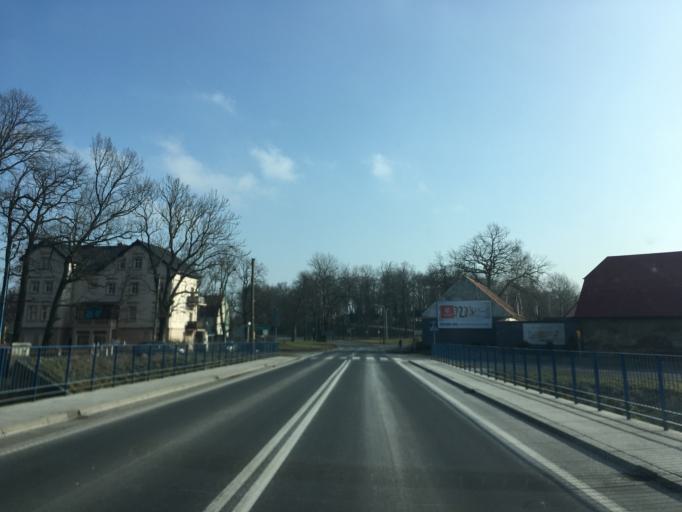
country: PL
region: Lower Silesian Voivodeship
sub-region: Powiat legnicki
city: Chojnow
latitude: 51.2680
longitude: 15.9257
